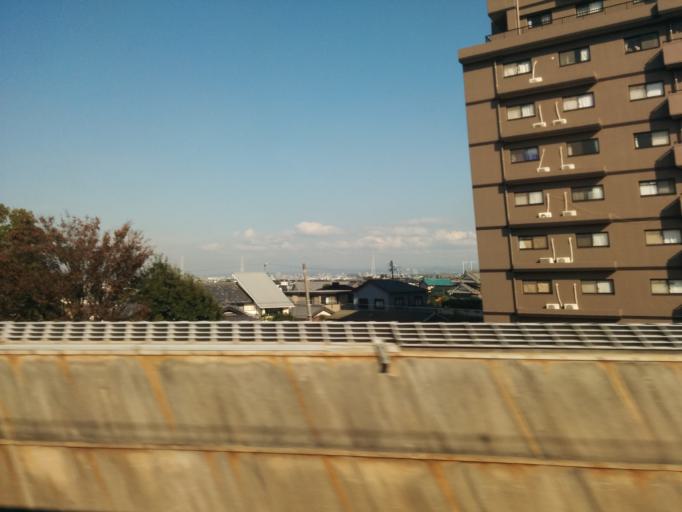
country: JP
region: Aichi
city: Okazaki
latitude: 34.8918
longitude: 137.1317
